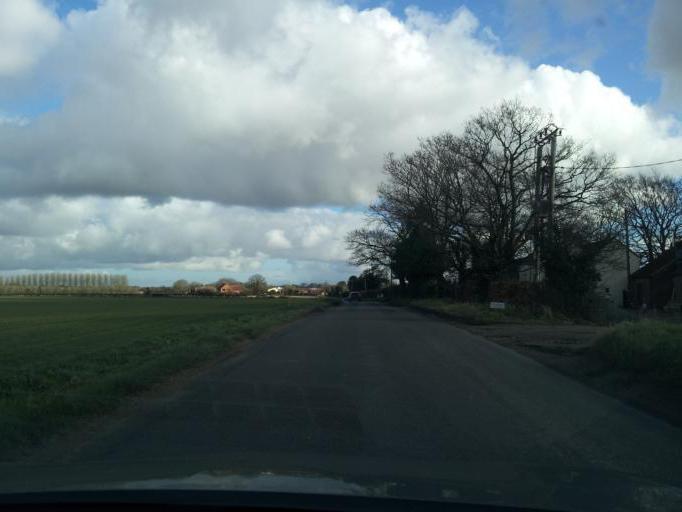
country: GB
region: England
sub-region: Norfolk
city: Mattishall
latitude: 52.6593
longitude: 1.0513
